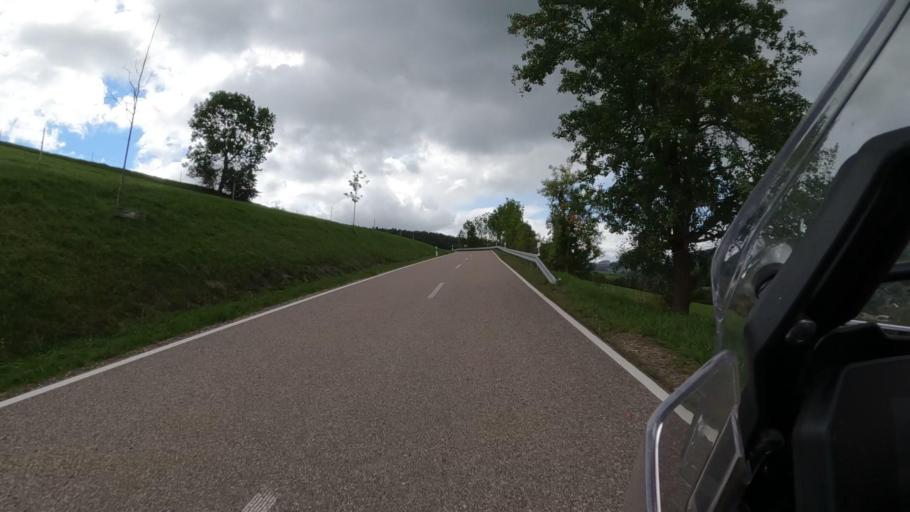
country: DE
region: Baden-Wuerttemberg
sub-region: Freiburg Region
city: Uhlingen-Birkendorf
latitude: 47.6991
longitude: 8.3467
